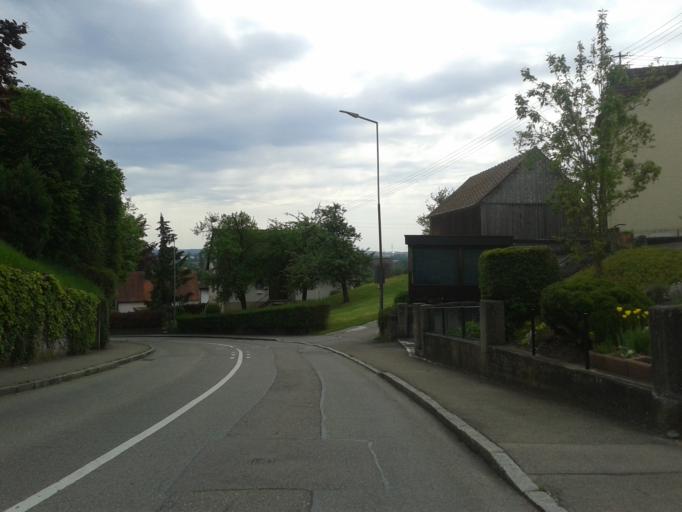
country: DE
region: Baden-Wuerttemberg
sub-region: Tuebingen Region
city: Erbach
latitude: 48.3218
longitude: 9.8832
